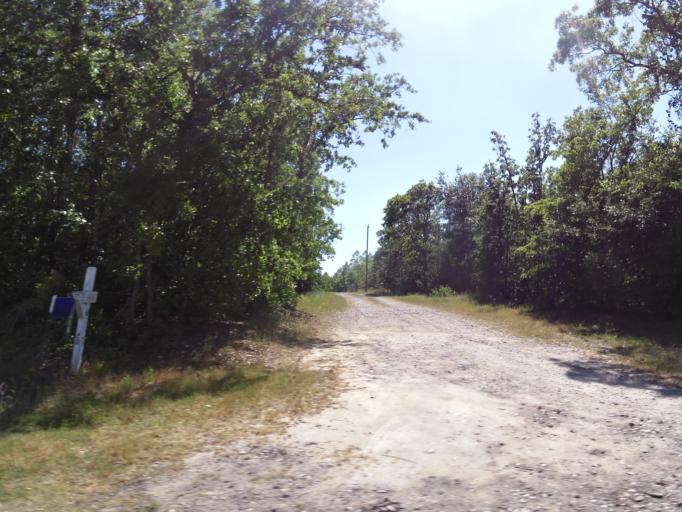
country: US
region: South Carolina
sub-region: Barnwell County
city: Williston
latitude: 33.4951
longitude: -81.5280
